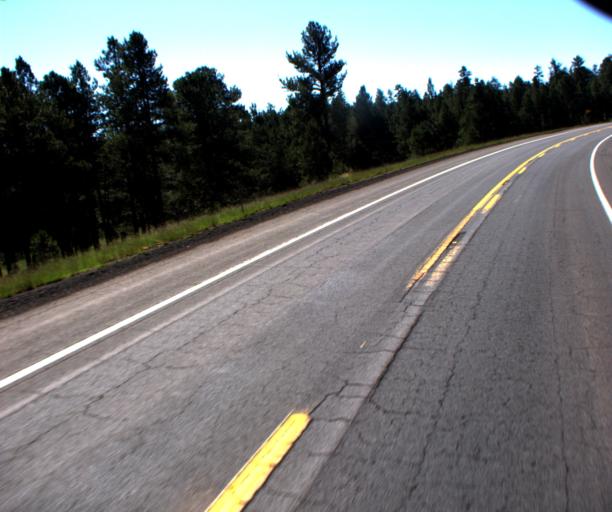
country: US
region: New Mexico
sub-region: Catron County
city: Reserve
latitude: 33.8193
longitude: -109.0742
